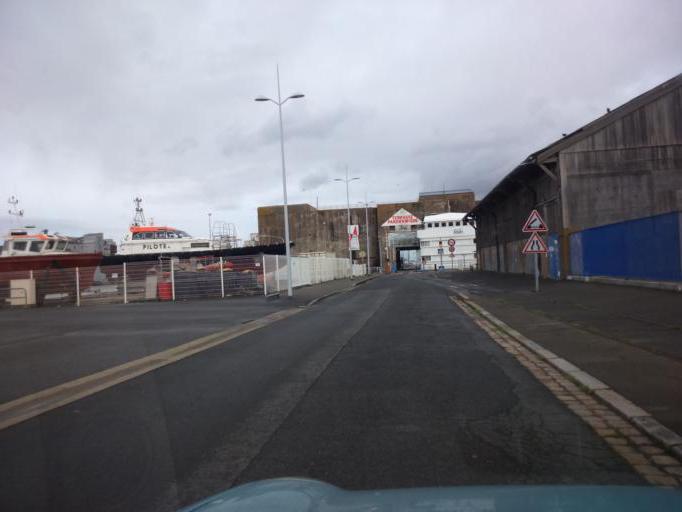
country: FR
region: Pays de la Loire
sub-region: Departement de la Loire-Atlantique
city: Saint-Nazaire
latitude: 47.2743
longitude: -2.1997
